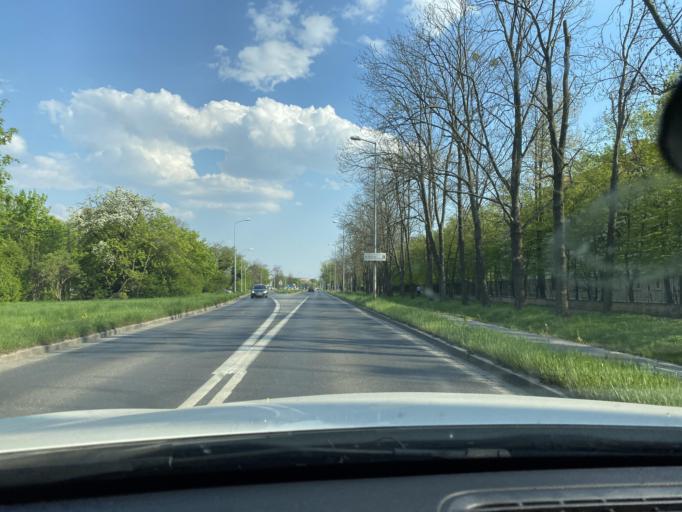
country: PL
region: Lower Silesian Voivodeship
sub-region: Powiat trzebnicki
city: Psary
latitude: 51.1501
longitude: 17.0185
